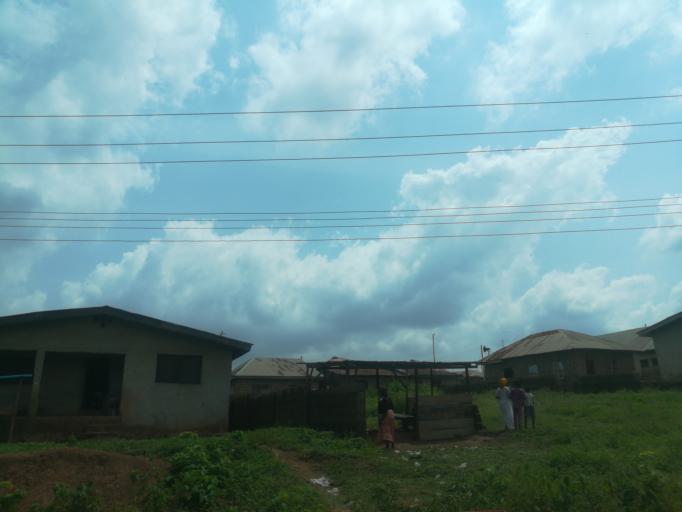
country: NG
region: Oyo
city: Moniya
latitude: 7.4712
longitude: 3.9572
